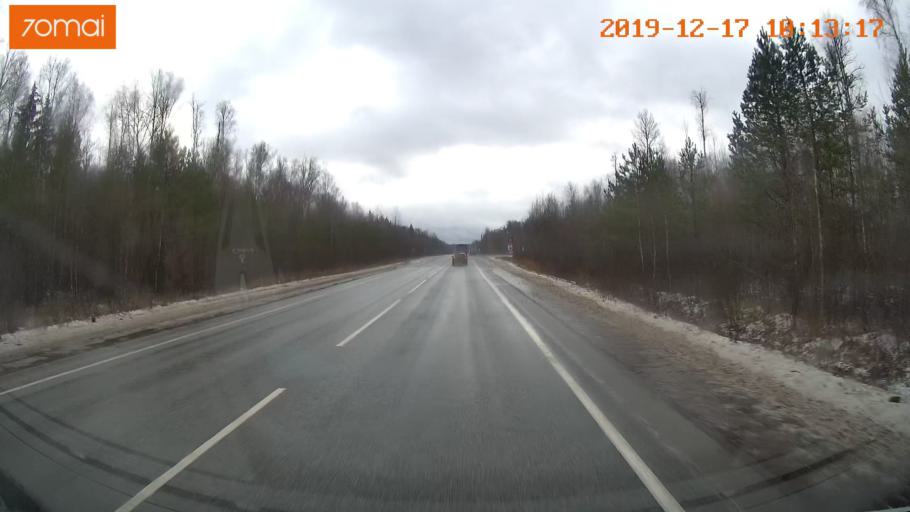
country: RU
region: Vladimir
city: Anopino
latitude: 55.8034
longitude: 40.6741
